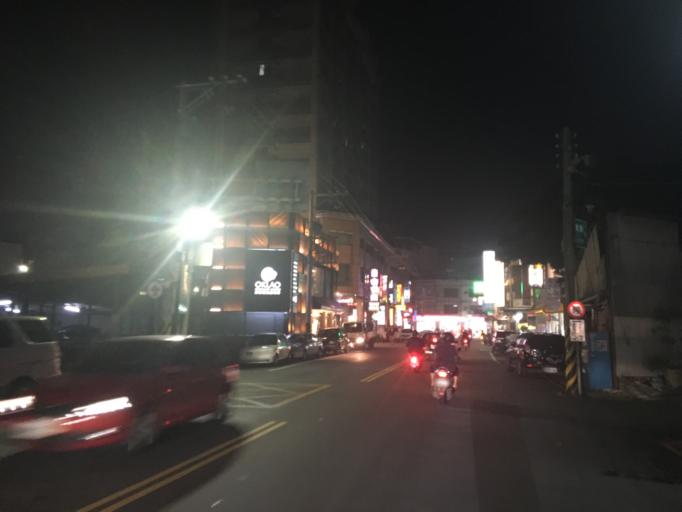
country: TW
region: Taiwan
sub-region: Hsinchu
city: Hsinchu
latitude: 24.8149
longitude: 120.9742
